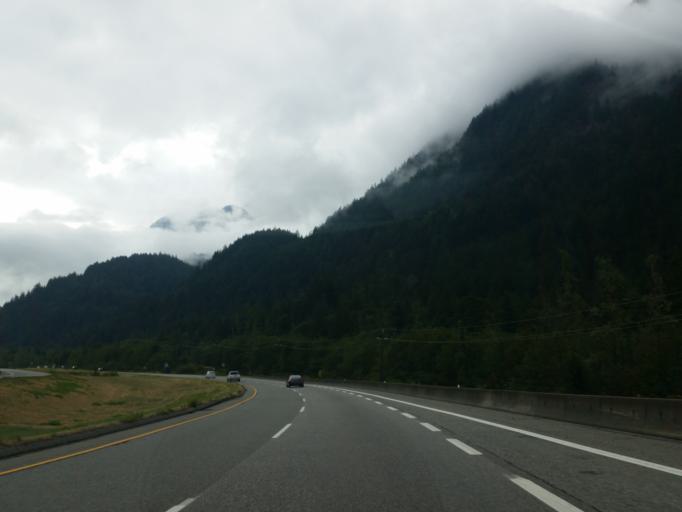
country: CA
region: British Columbia
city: Hope
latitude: 49.3614
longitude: -121.5158
